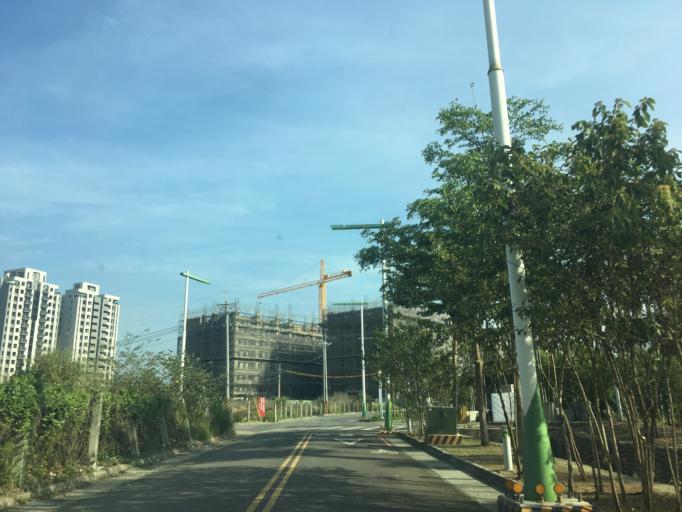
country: TW
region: Taiwan
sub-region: Taichung City
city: Taichung
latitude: 24.1949
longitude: 120.7086
